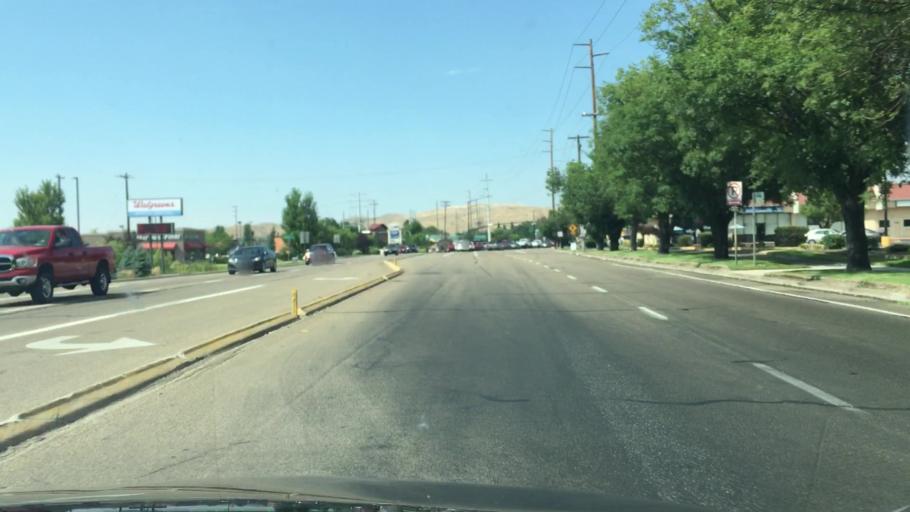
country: US
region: Idaho
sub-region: Ada County
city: Garden City
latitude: 43.6662
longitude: -116.2793
